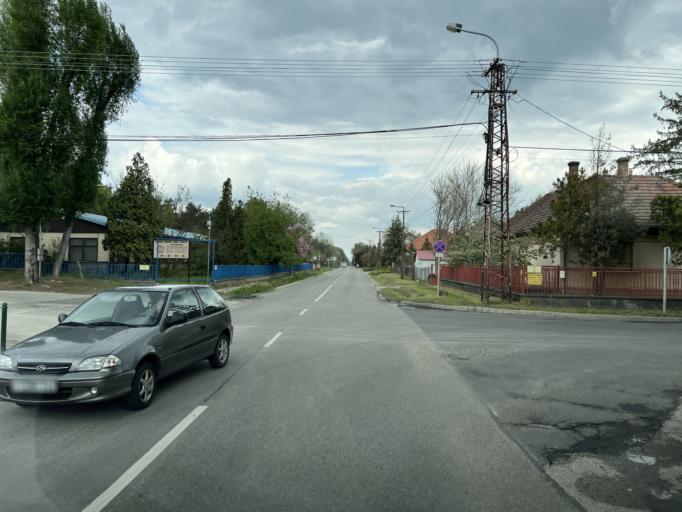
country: HU
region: Pest
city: Hernad
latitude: 47.1717
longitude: 19.4139
